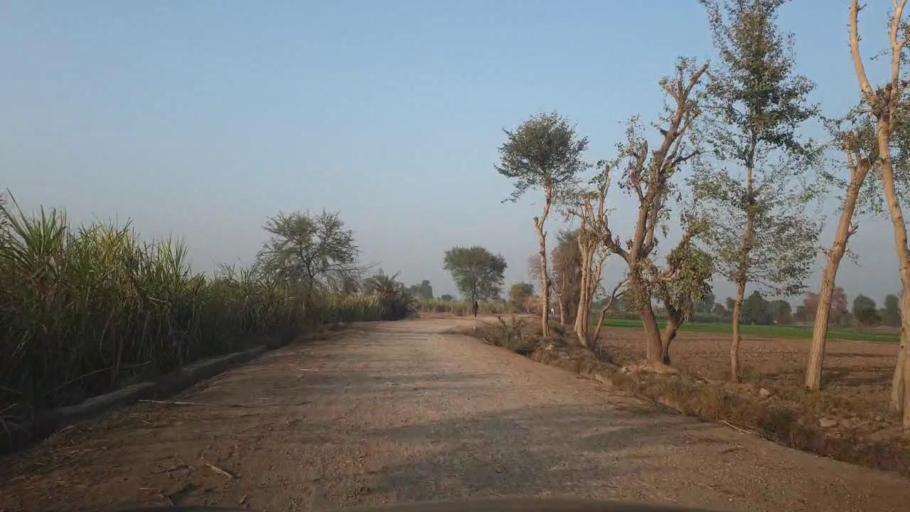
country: PK
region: Sindh
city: Ubauro
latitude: 28.3244
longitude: 69.7762
